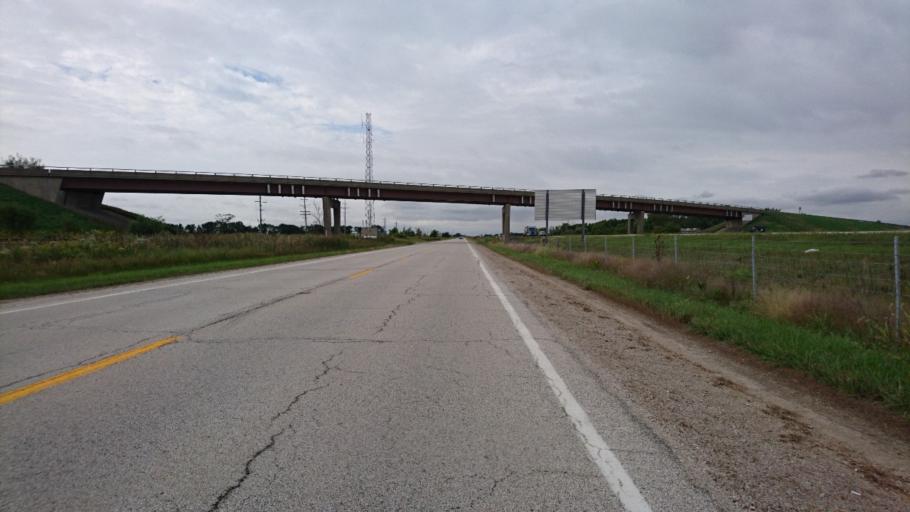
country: US
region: Illinois
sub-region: Livingston County
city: Dwight
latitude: 41.0657
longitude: -88.4622
